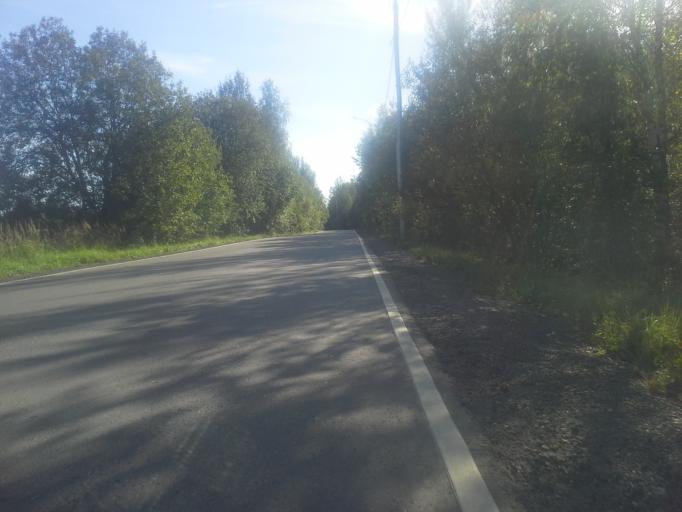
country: RU
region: Moskovskaya
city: Kievskij
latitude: 55.3558
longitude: 36.9542
